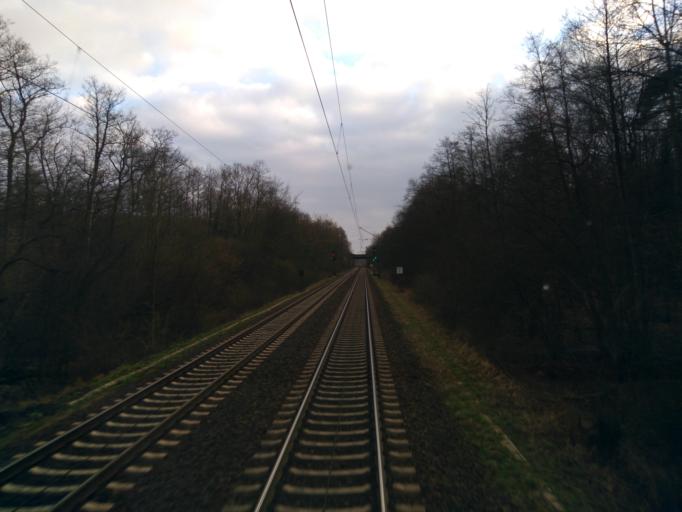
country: DE
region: Lower Saxony
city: Deutsch Evern
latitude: 53.2133
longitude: 10.4293
